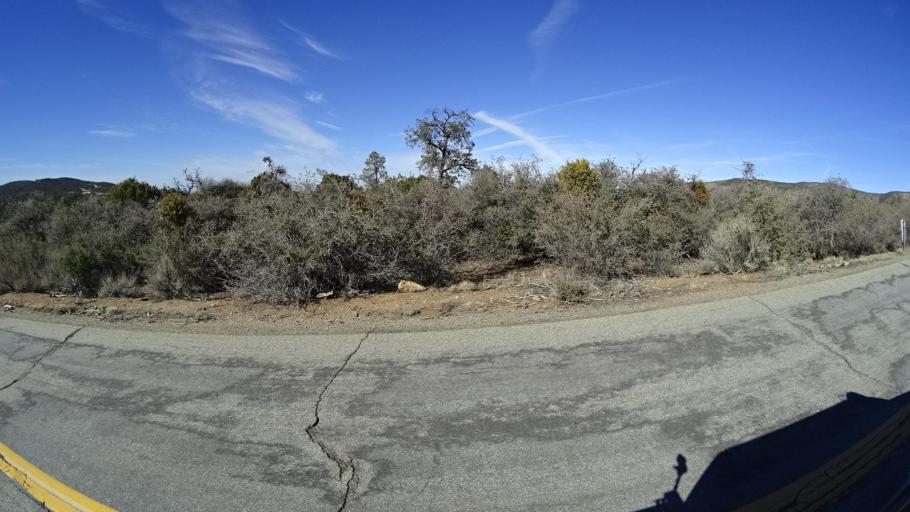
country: US
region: California
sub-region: Kern County
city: Pine Mountain Club
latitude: 34.8724
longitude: -119.2713
